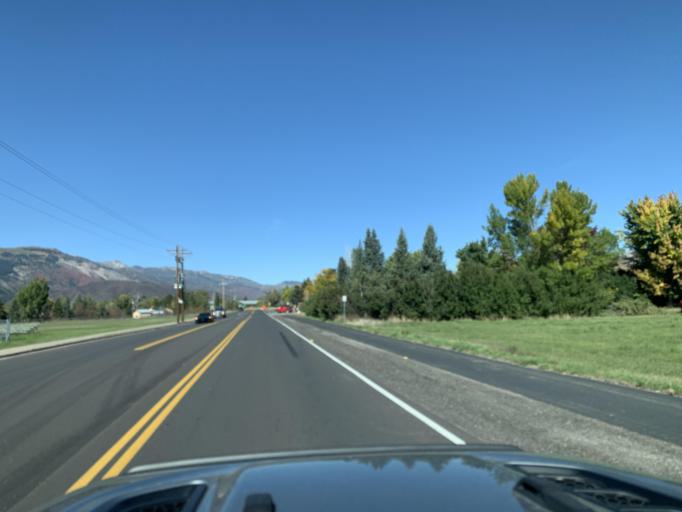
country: US
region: Utah
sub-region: Weber County
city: Wolf Creek
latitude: 41.3097
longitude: -111.8330
